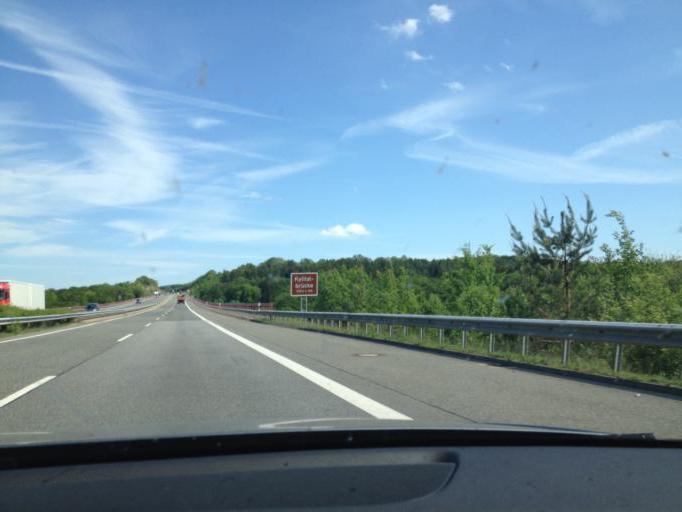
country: DE
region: Rheinland-Pfalz
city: Etteldorf
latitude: 50.0207
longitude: 6.5692
